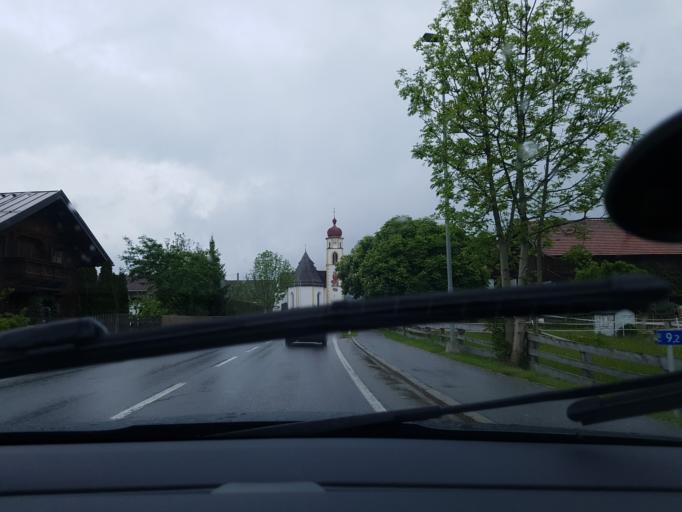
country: AT
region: Tyrol
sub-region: Politischer Bezirk Imst
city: Mieming
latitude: 47.3046
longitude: 10.9691
